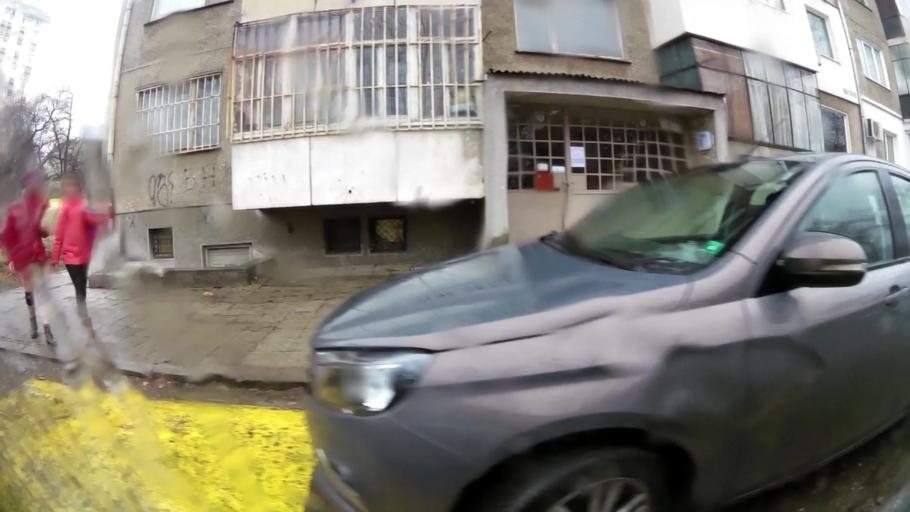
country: BG
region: Sofia-Capital
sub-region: Stolichna Obshtina
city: Sofia
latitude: 42.6592
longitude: 23.3758
